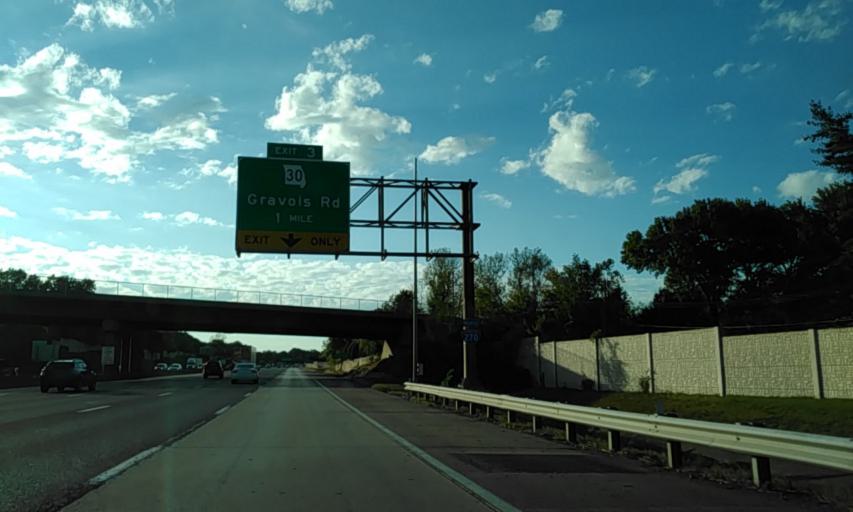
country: US
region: Missouri
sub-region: Saint Louis County
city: Sappington
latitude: 38.5154
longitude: -90.3792
